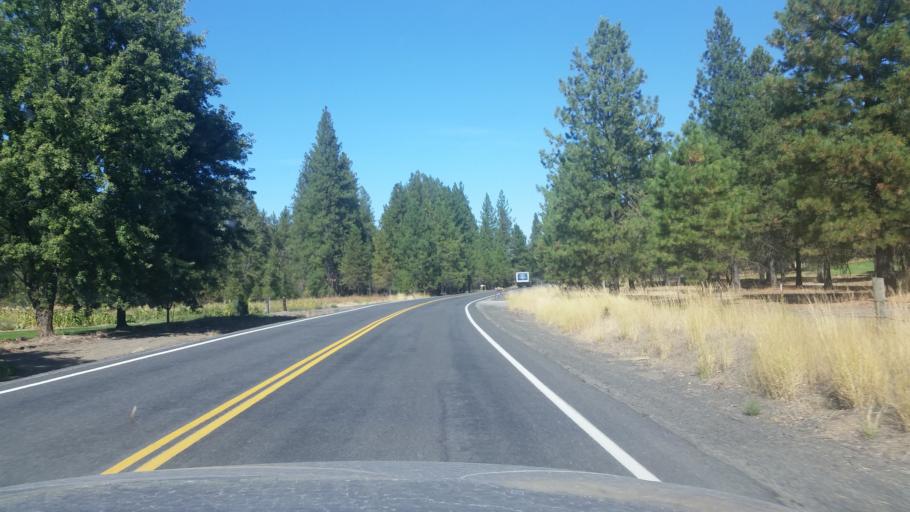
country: US
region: Washington
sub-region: Spokane County
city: Spokane
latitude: 47.5851
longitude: -117.4555
